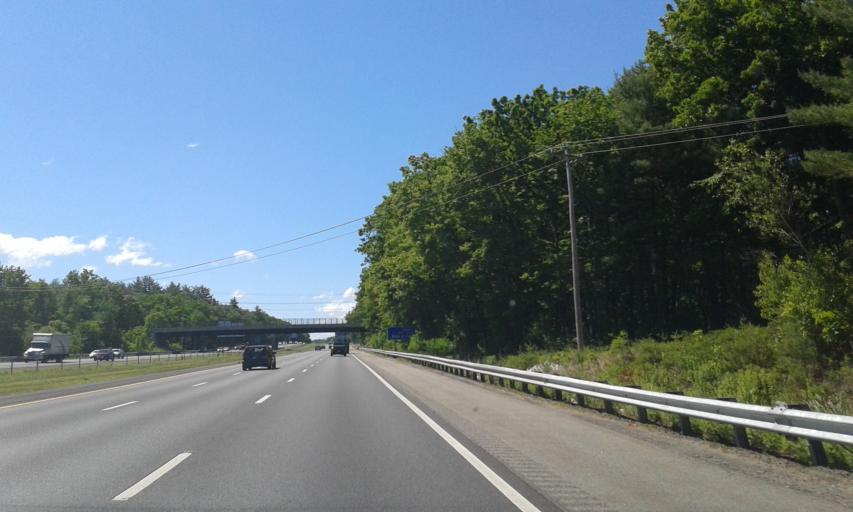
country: US
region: Massachusetts
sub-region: Middlesex County
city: Billerica
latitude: 42.5780
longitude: -71.3072
